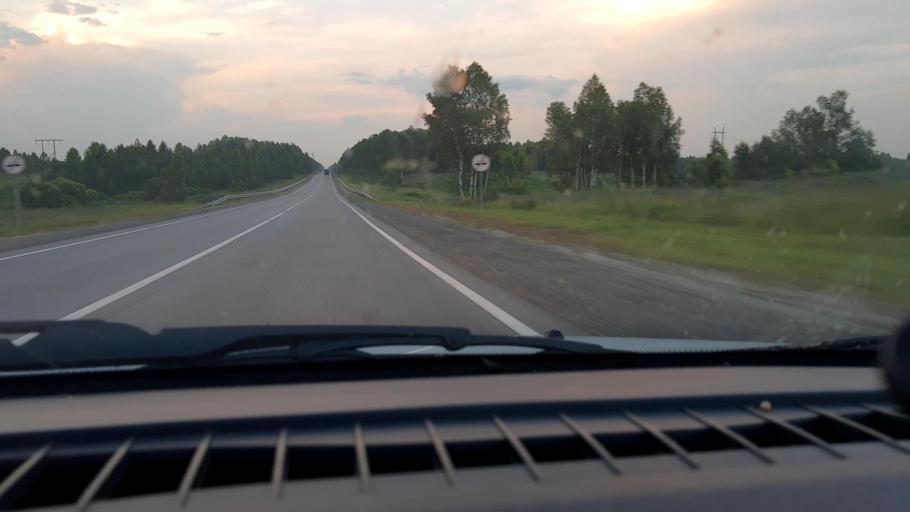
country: RU
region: Nizjnij Novgorod
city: Arzamas
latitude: 55.5491
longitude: 43.9408
